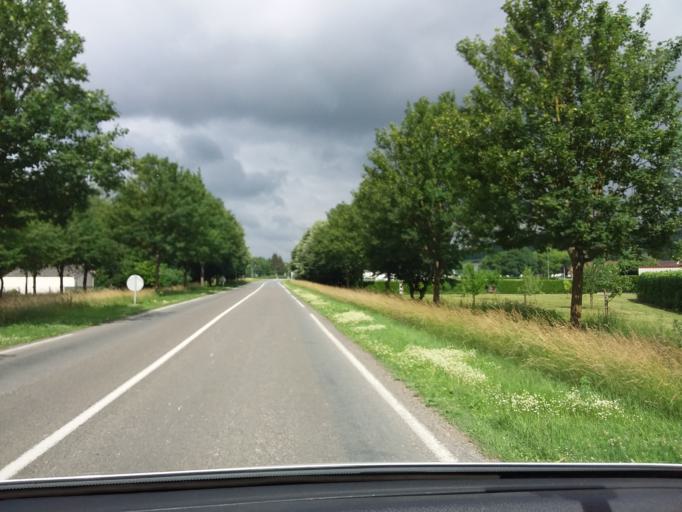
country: FR
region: Picardie
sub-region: Departement de l'Aisne
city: Bucy-le-Long
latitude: 49.3865
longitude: 3.3974
